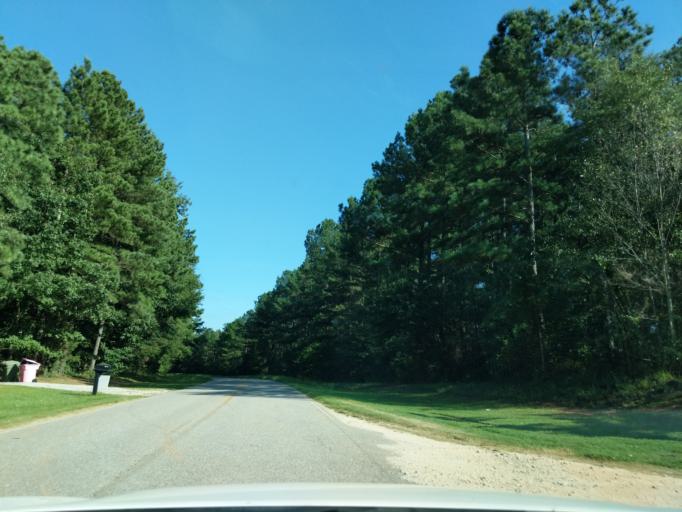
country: US
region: Georgia
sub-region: Oglethorpe County
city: Lexington
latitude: 33.9207
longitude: -83.0260
